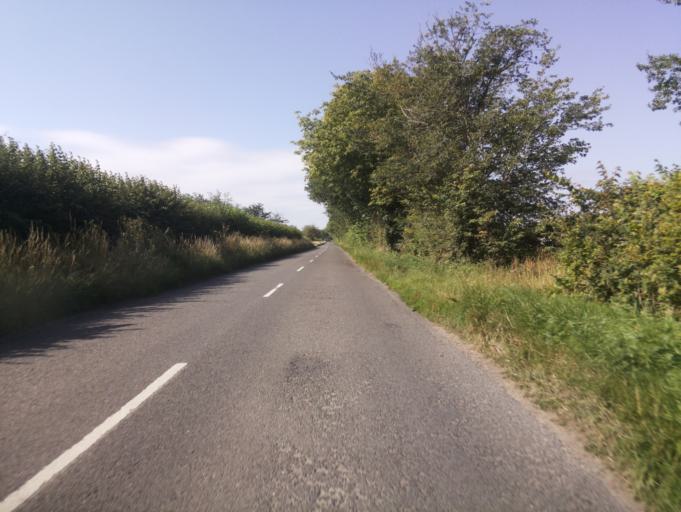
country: GB
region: England
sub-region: Oxfordshire
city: Bampton
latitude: 51.7323
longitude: -1.5051
